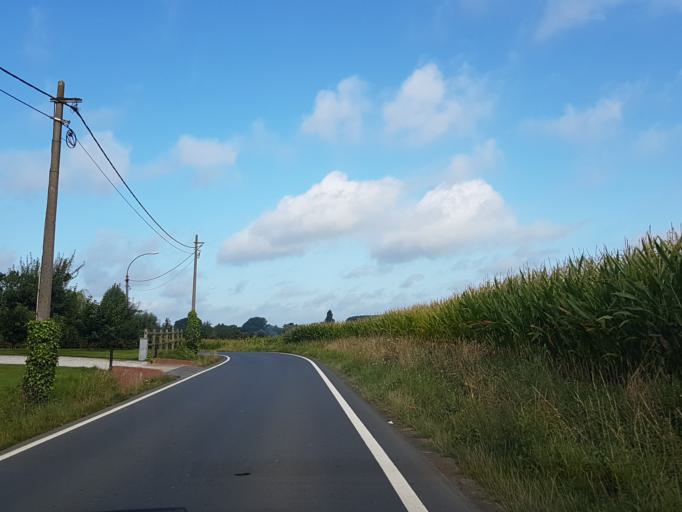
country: BE
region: Flanders
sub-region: Provincie Oost-Vlaanderen
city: Lovendegem
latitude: 51.0691
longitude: 3.6078
